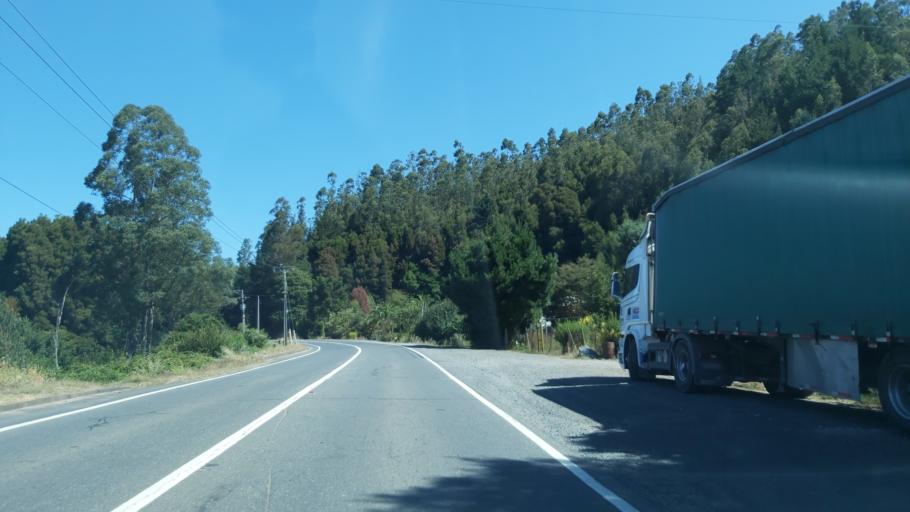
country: CL
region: Biobio
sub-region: Provincia de Concepcion
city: Chiguayante
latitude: -36.9297
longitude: -73.0499
